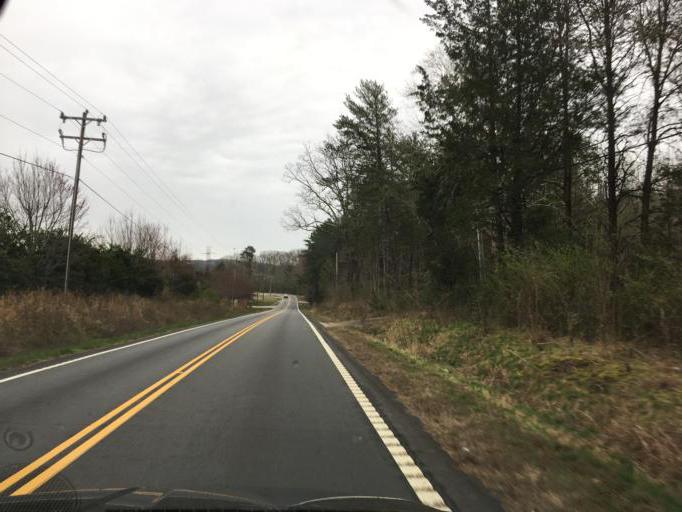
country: US
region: South Carolina
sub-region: Greenville County
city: Berea
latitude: 34.9178
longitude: -82.4741
